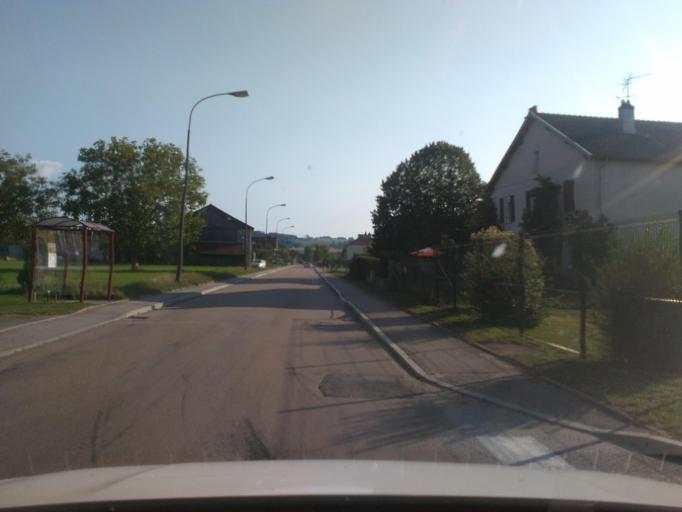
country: FR
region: Lorraine
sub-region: Departement des Vosges
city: Corcieux
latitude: 48.1782
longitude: 6.8838
